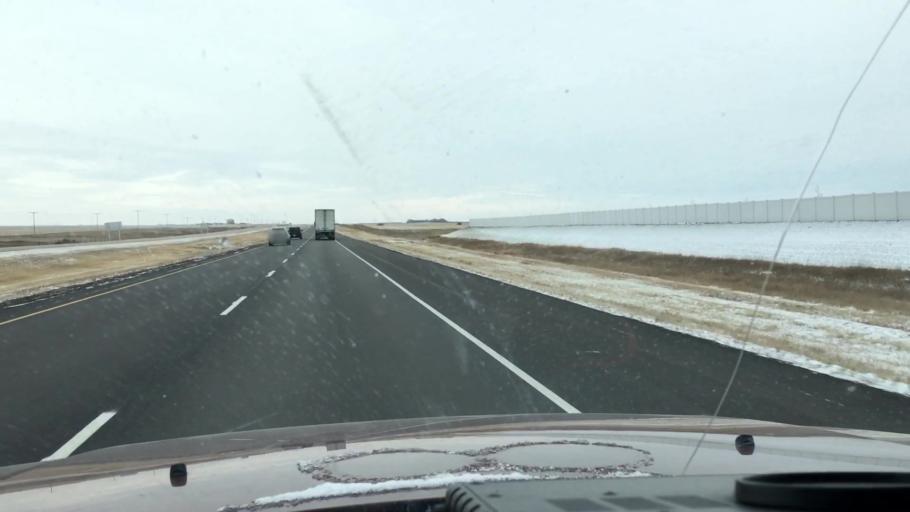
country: CA
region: Saskatchewan
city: Saskatoon
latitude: 51.8042
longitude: -106.4921
